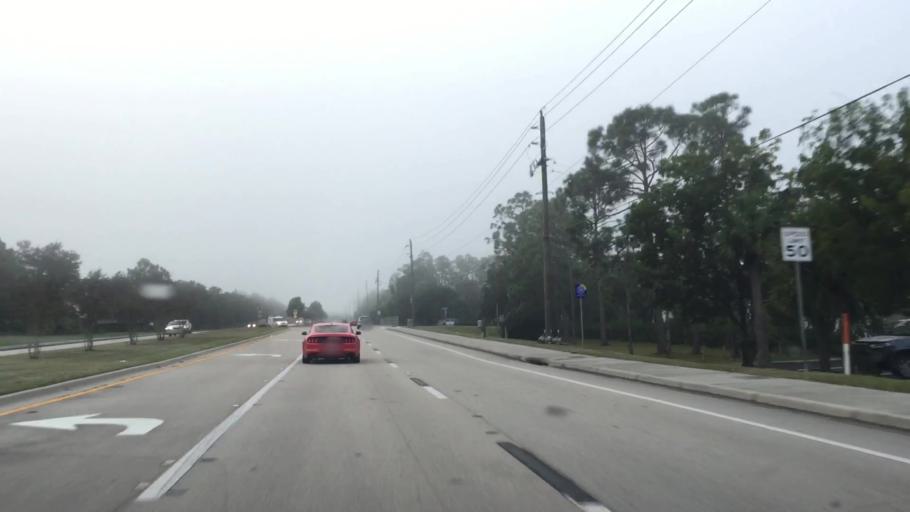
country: US
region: Florida
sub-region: Lee County
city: Gateway
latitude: 26.5633
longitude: -81.7874
